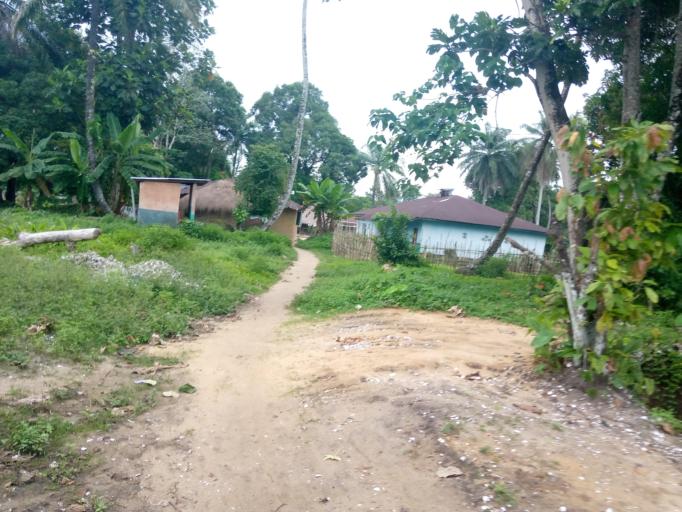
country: SL
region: Southern Province
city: Bonthe
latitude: 7.5223
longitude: -12.5018
